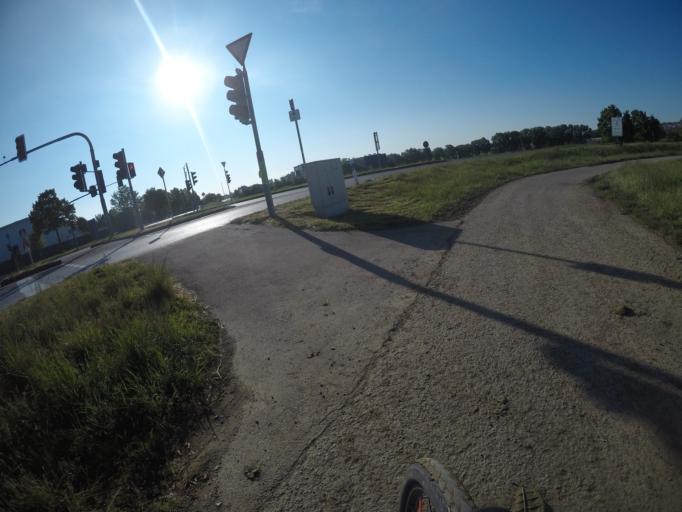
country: DE
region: Baden-Wuerttemberg
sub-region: Regierungsbezirk Stuttgart
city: Leinfelden-Echterdingen
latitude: 48.6783
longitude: 9.1891
